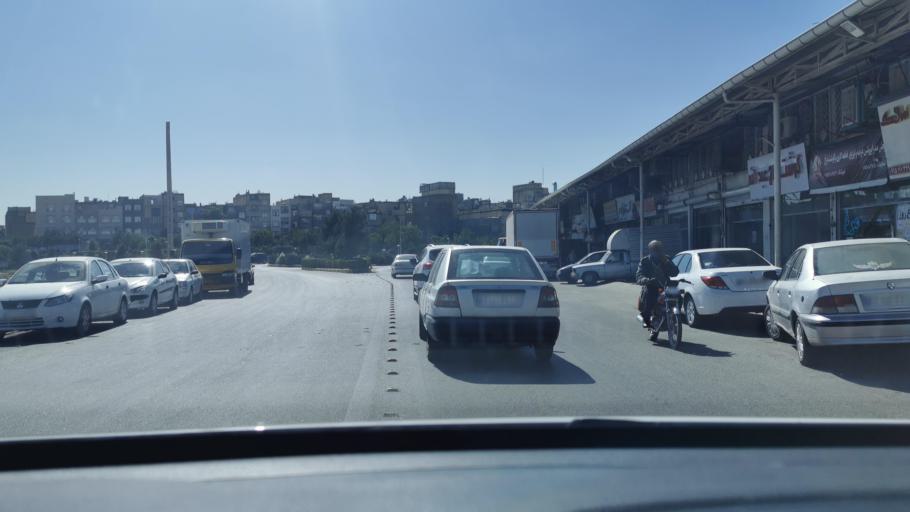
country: IR
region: Razavi Khorasan
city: Mashhad
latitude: 36.3349
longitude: 59.6187
